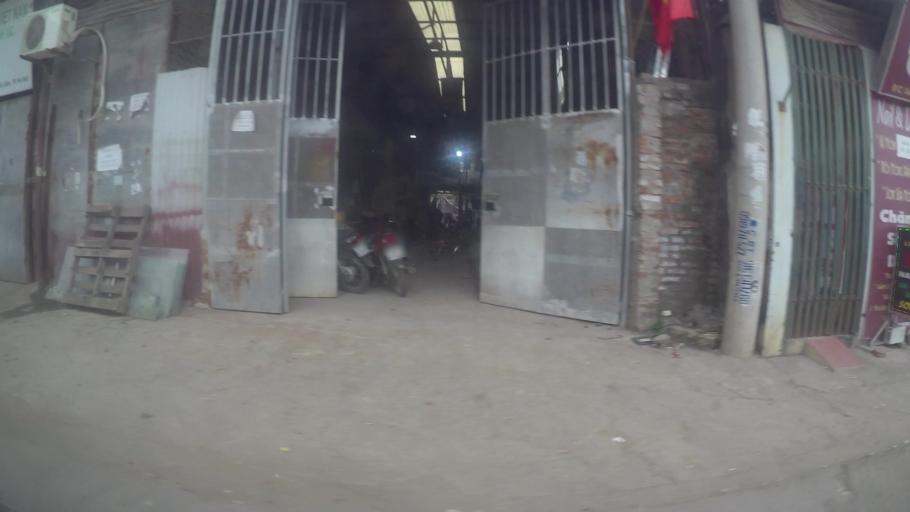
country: VN
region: Ha Noi
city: Cau Dien
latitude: 21.0348
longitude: 105.7473
